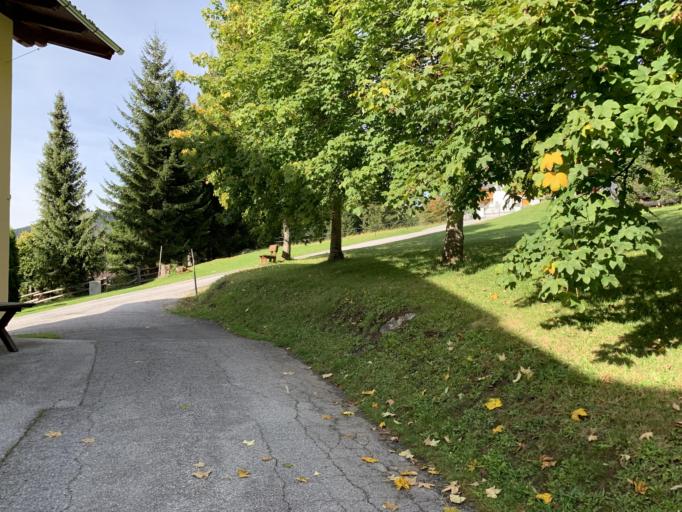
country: AT
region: Styria
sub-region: Politischer Bezirk Liezen
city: Schladming
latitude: 47.4306
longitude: 13.6449
